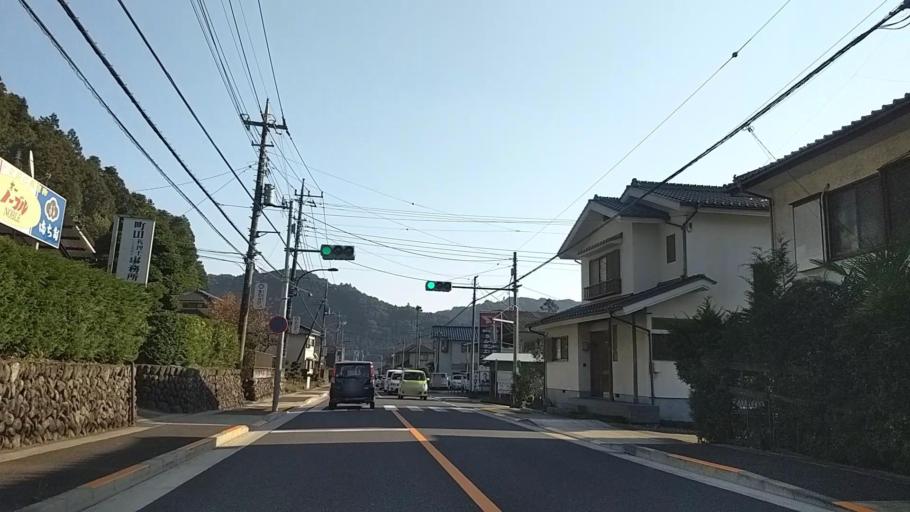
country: JP
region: Tokyo
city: Ome
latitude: 35.7859
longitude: 139.2312
